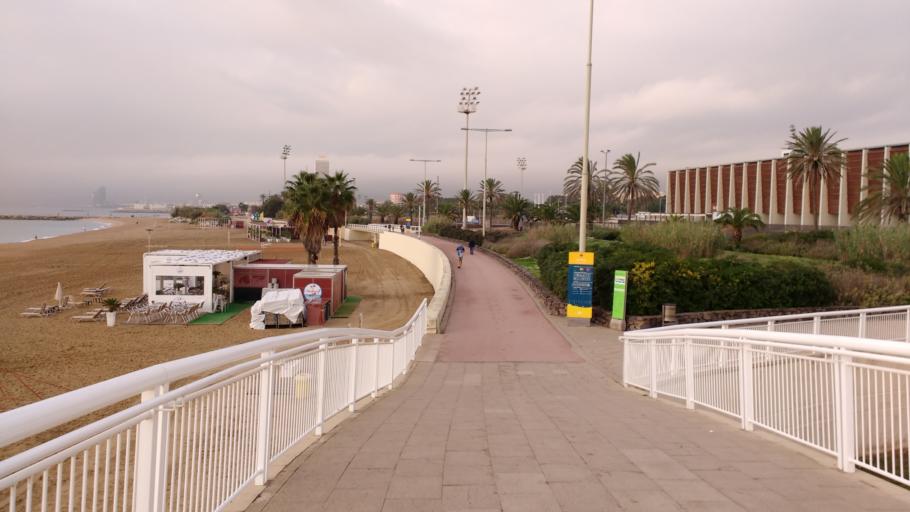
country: ES
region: Catalonia
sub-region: Provincia de Barcelona
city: Sant Marti
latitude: 41.4001
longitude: 2.2135
